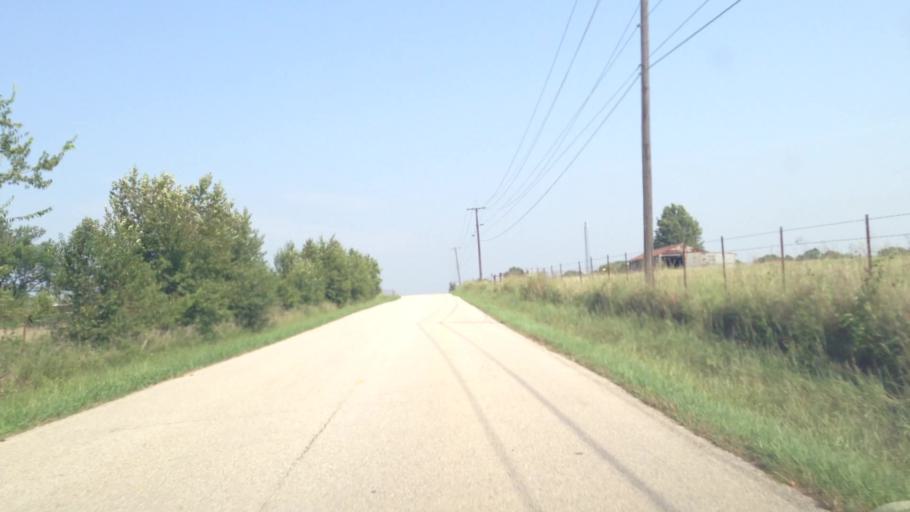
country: US
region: Oklahoma
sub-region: Craig County
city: Vinita
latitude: 36.6505
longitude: -95.1256
